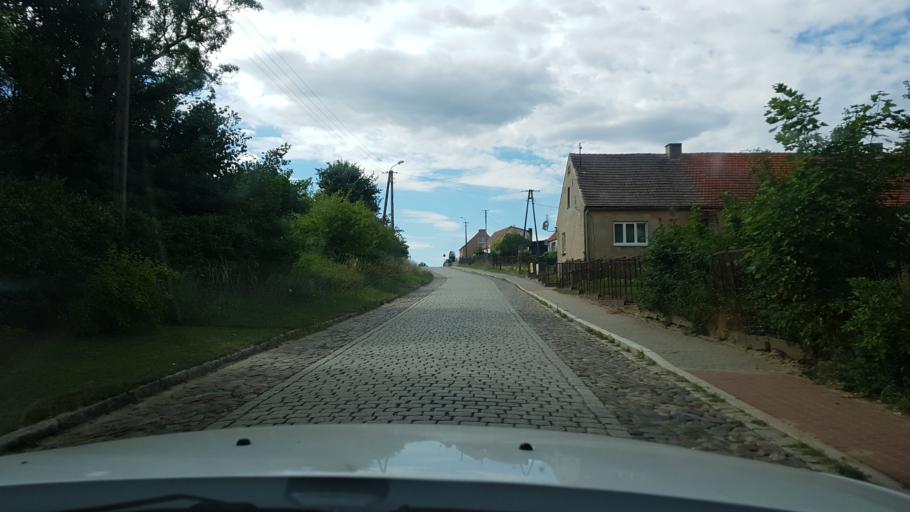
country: PL
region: West Pomeranian Voivodeship
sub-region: Powiat drawski
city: Wierzchowo
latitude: 53.4807
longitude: 16.0492
